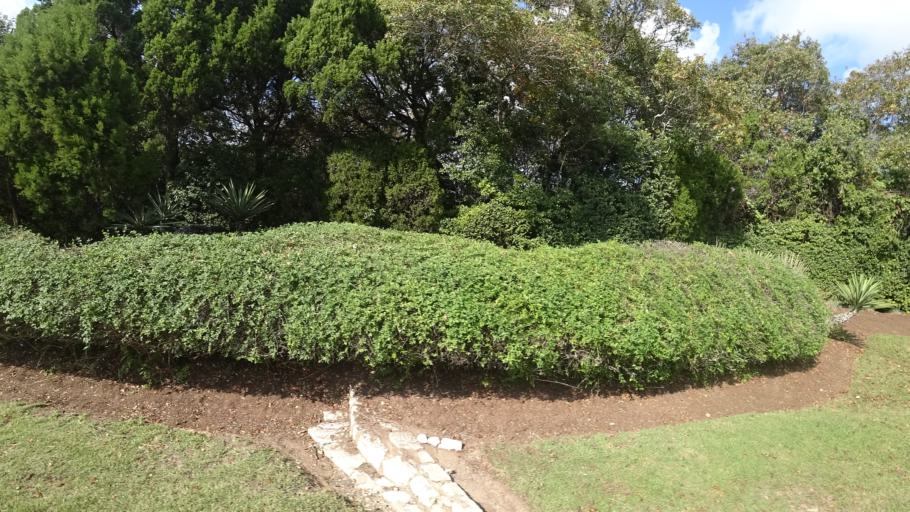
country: US
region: Texas
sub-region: Travis County
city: Lost Creek
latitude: 30.3040
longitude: -97.8426
